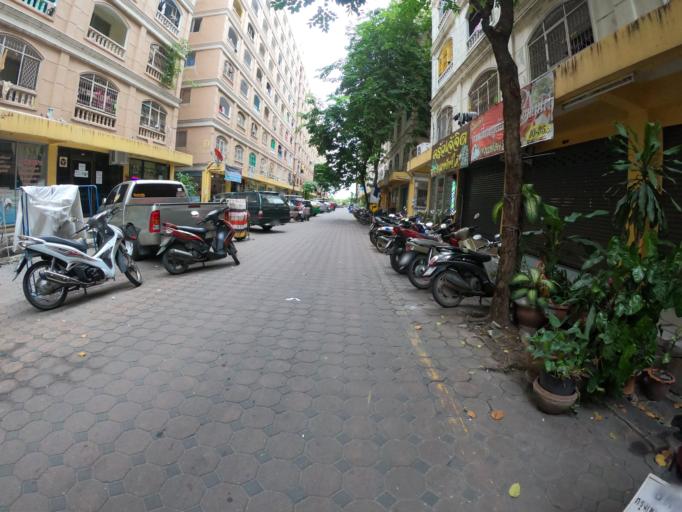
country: TH
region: Bangkok
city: Bang Na
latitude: 13.6709
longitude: 100.6812
